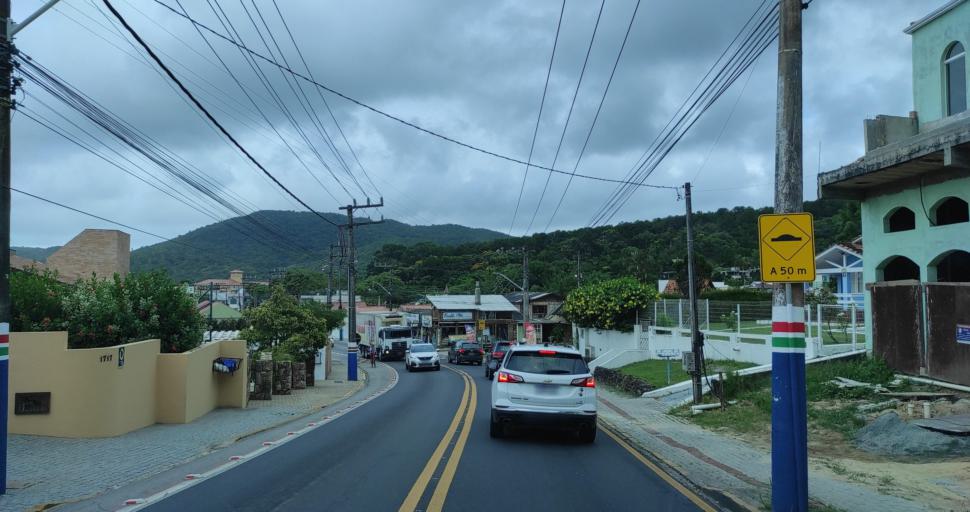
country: BR
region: Santa Catarina
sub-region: Porto Belo
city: Porto Belo
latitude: -27.1575
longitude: -48.5495
